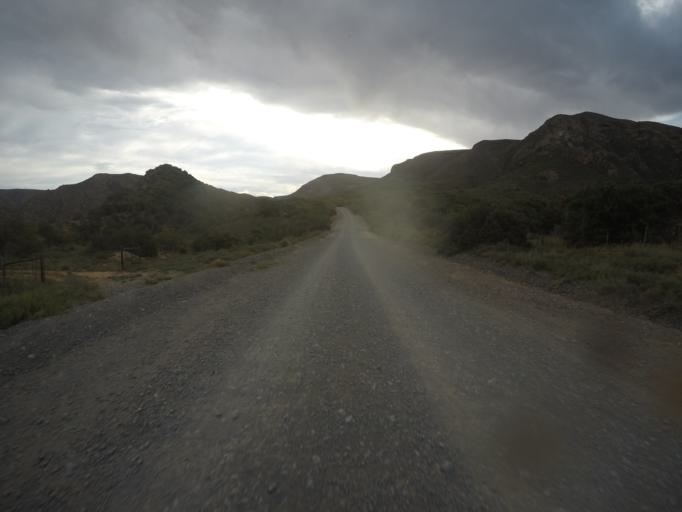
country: ZA
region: Eastern Cape
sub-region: Cacadu District Municipality
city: Willowmore
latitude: -33.5186
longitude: 23.8299
